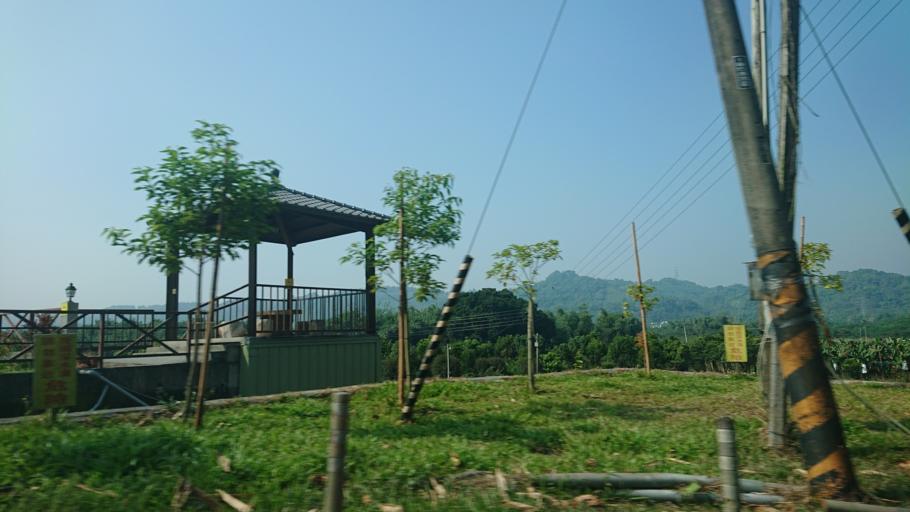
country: TW
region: Taiwan
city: Lugu
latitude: 23.7039
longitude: 120.6628
